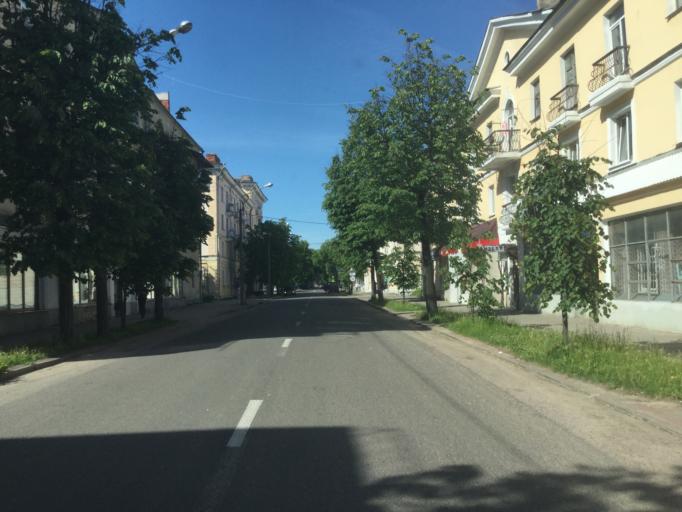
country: BY
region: Vitebsk
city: Vitebsk
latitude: 55.1925
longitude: 30.1916
